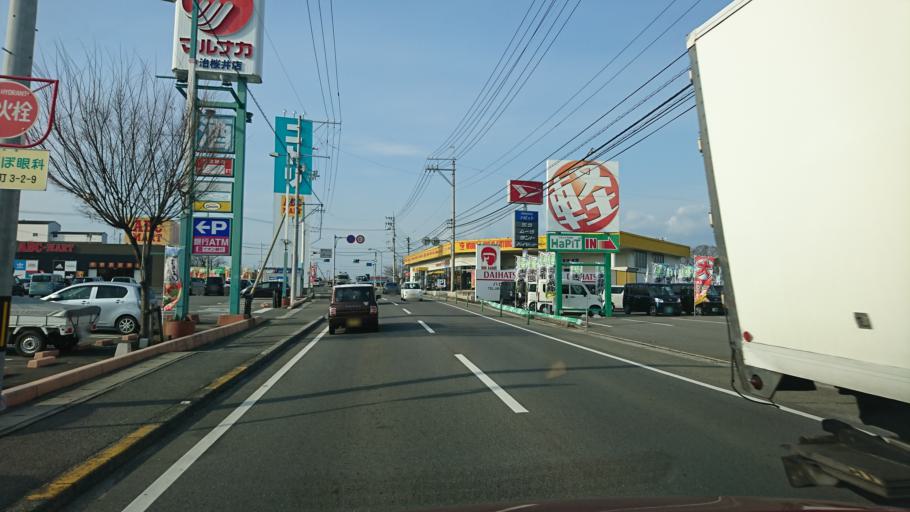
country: JP
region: Ehime
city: Saijo
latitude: 34.0364
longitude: 133.0331
